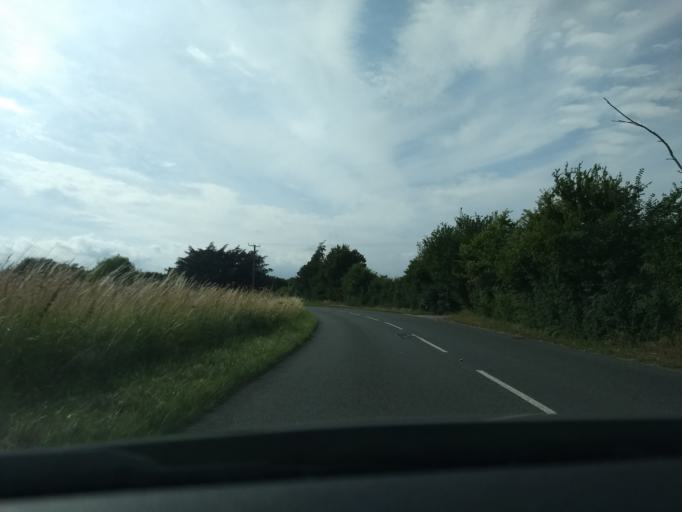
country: GB
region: England
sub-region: Suffolk
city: Shotley Gate
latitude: 51.9904
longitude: 1.2014
